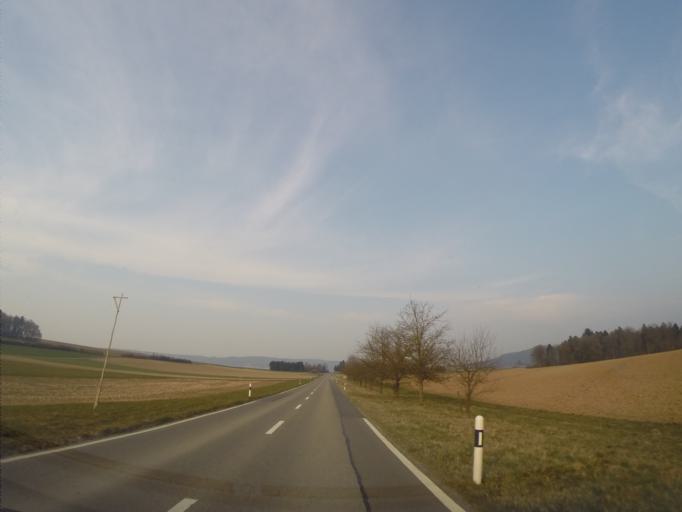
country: CH
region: Thurgau
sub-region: Frauenfeld District
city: Diessenhofen
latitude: 47.6580
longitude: 8.7329
